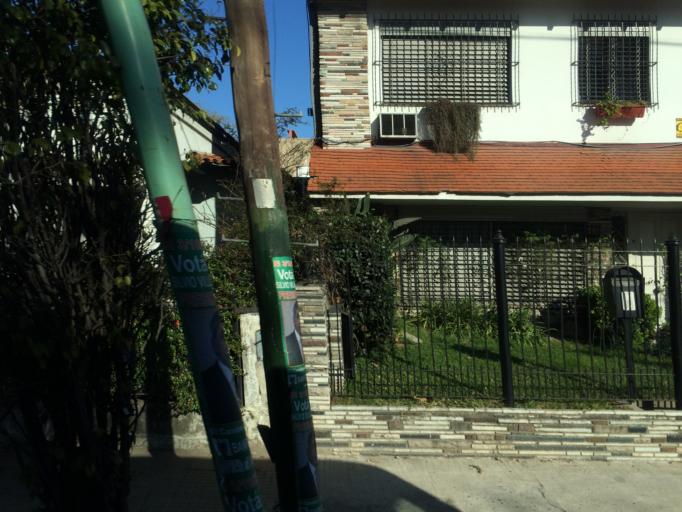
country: AR
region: Buenos Aires
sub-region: Partido de Lomas de Zamora
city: Lomas de Zamora
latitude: -34.7491
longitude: -58.3944
